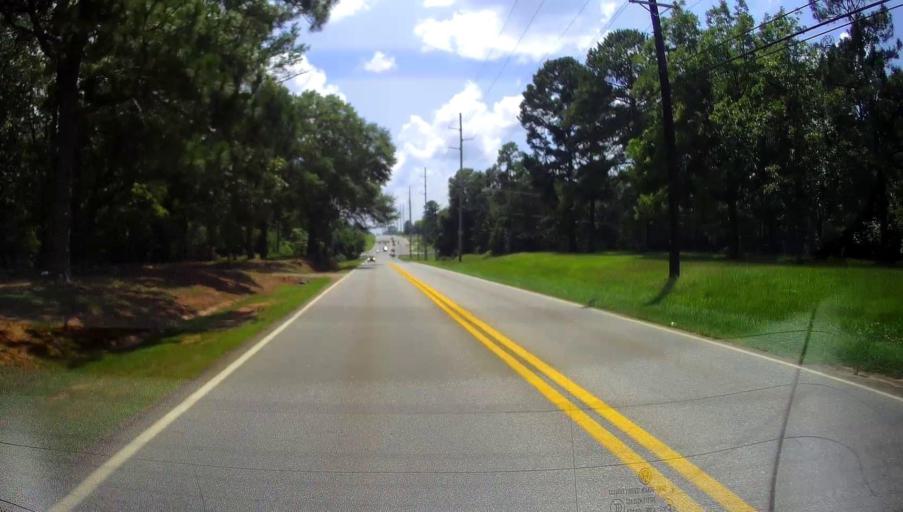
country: US
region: Georgia
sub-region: Houston County
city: Centerville
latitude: 32.6358
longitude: -83.7089
